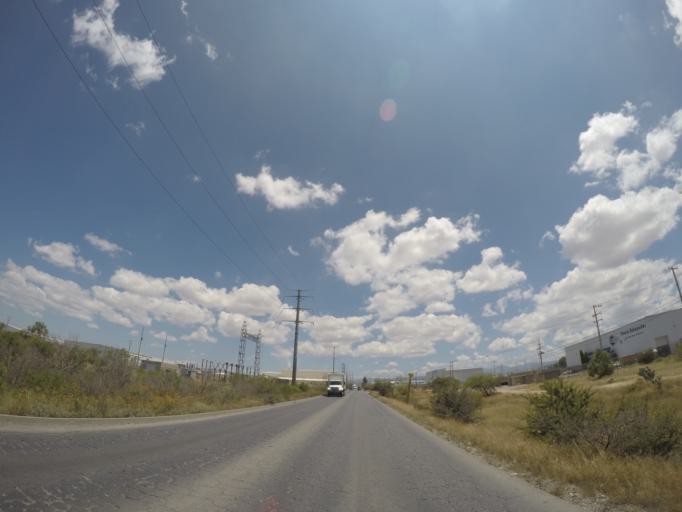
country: MX
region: San Luis Potosi
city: La Pila
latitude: 22.0466
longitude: -100.8753
